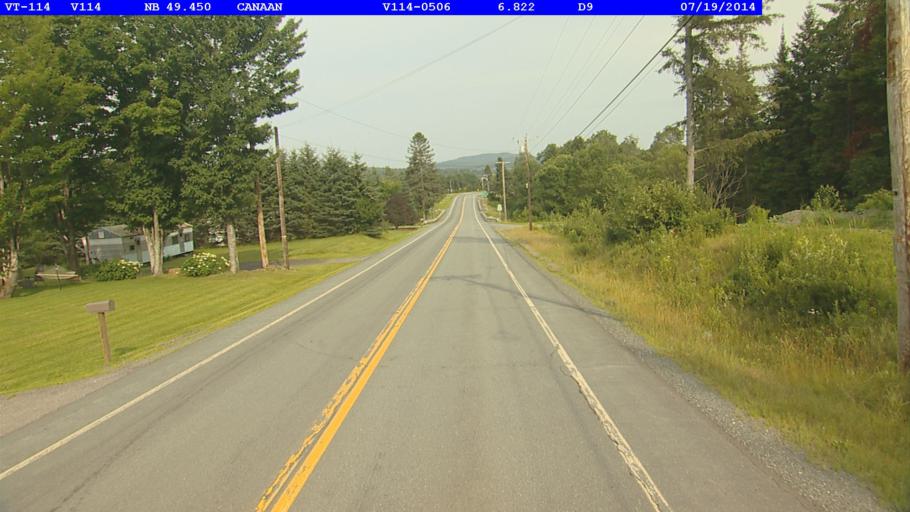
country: US
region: New Hampshire
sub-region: Coos County
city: Colebrook
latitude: 45.0079
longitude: -71.5600
